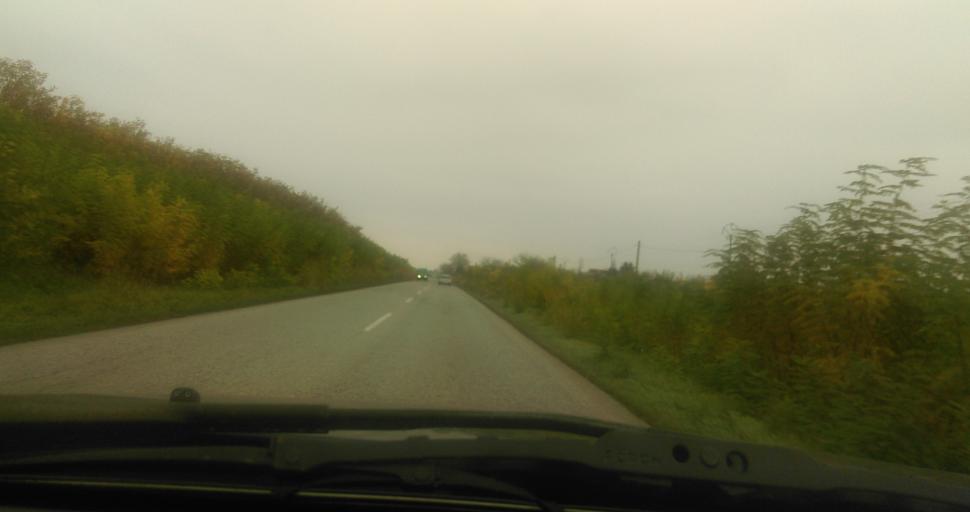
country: RS
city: Backo Gradiste
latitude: 45.5746
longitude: 20.0246
